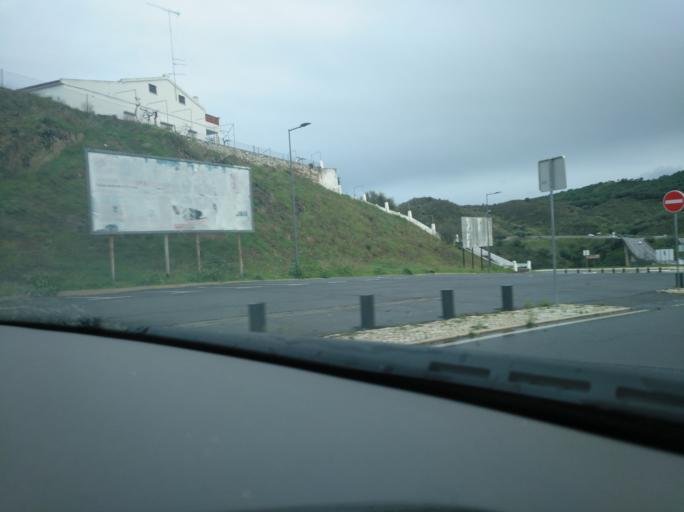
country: PT
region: Beja
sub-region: Mertola
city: Mertola
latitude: 37.6425
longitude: -7.6600
